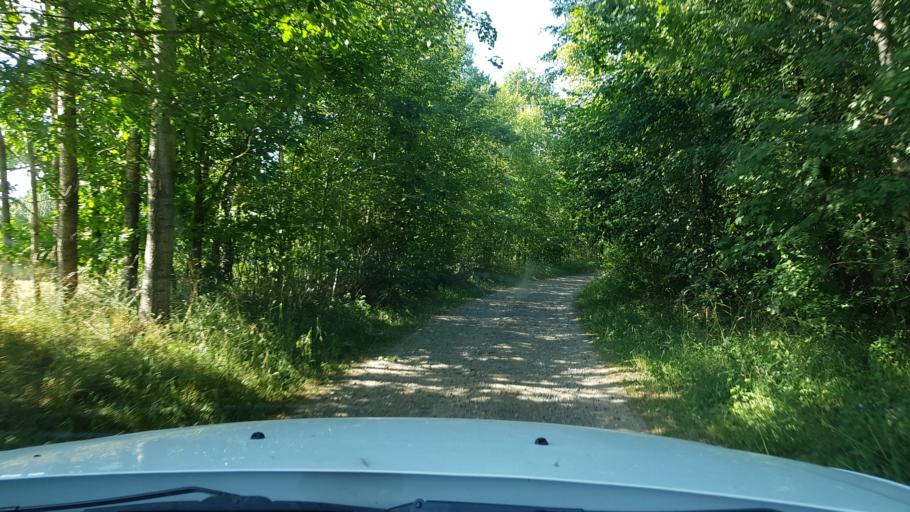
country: PL
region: West Pomeranian Voivodeship
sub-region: Powiat swidwinski
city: Polczyn-Zdroj
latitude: 53.6585
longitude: 16.0486
